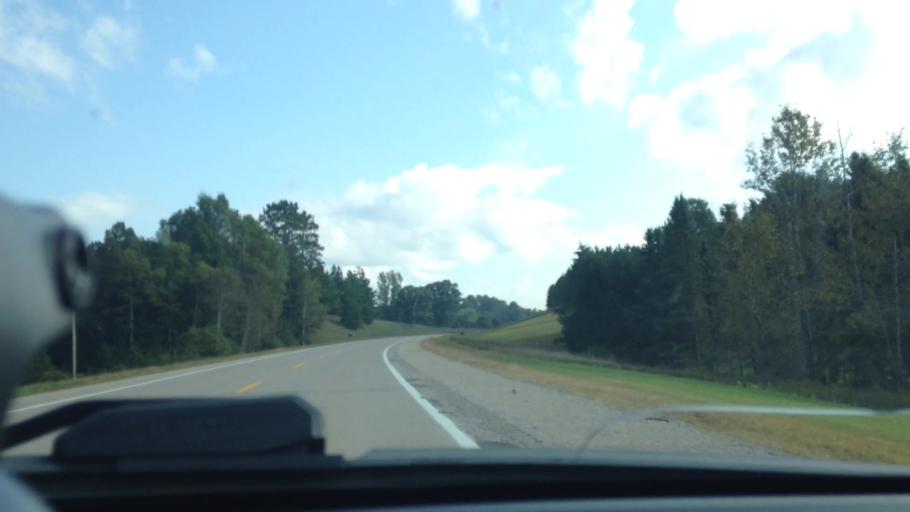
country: US
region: Michigan
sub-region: Dickinson County
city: Norway
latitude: 45.7631
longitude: -87.9197
